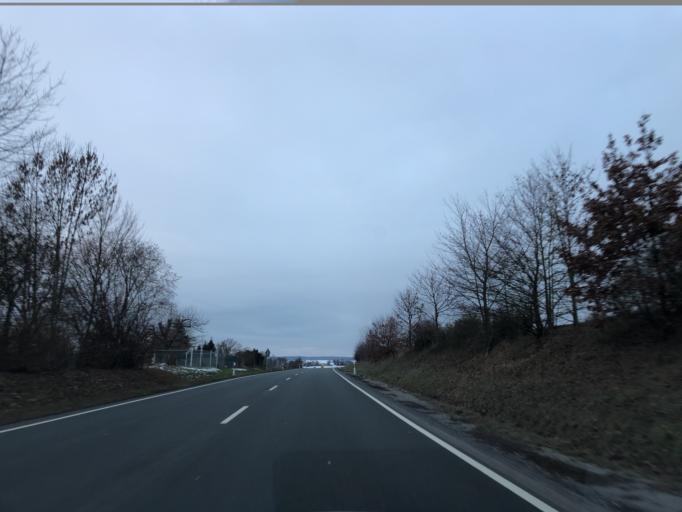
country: DE
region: Bavaria
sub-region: Regierungsbezirk Unterfranken
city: Esselbach
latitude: 49.8545
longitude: 9.5298
